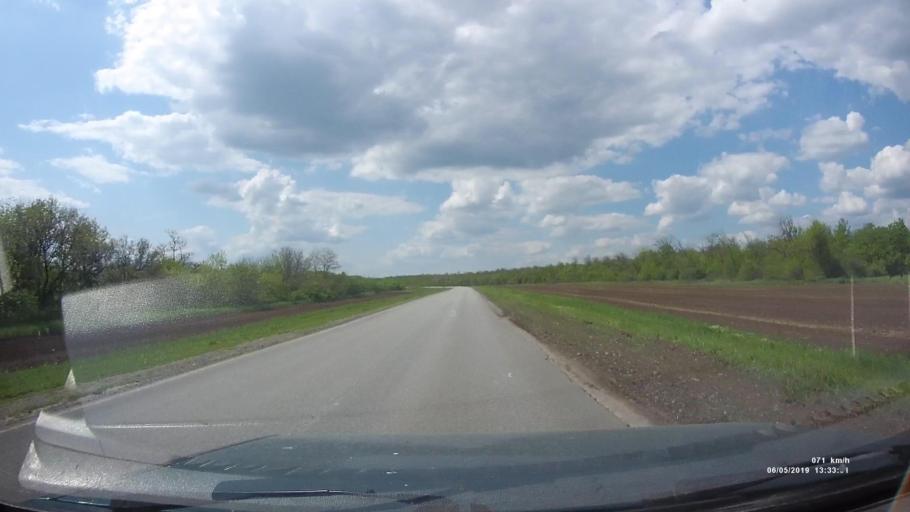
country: RU
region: Rostov
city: Ust'-Donetskiy
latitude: 47.6919
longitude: 40.7729
